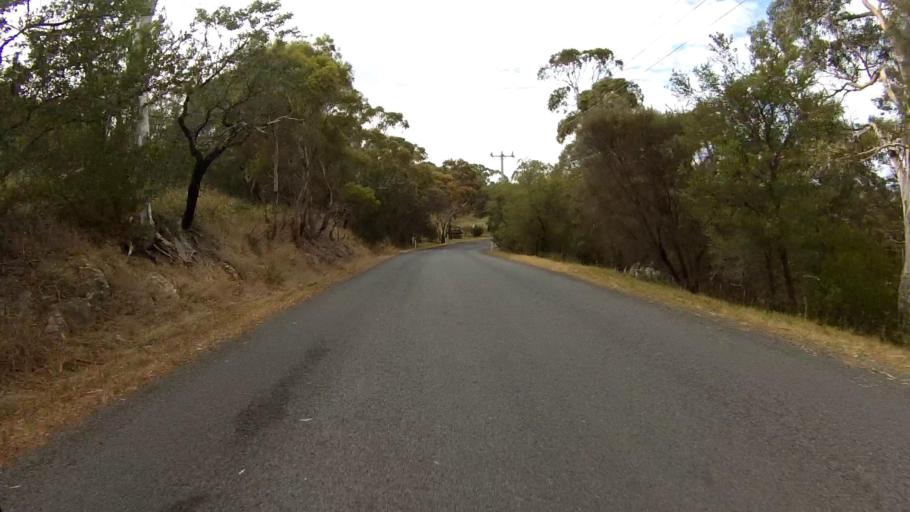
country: AU
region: Tasmania
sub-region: Glenorchy
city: Goodwood
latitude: -42.8004
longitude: 147.2908
